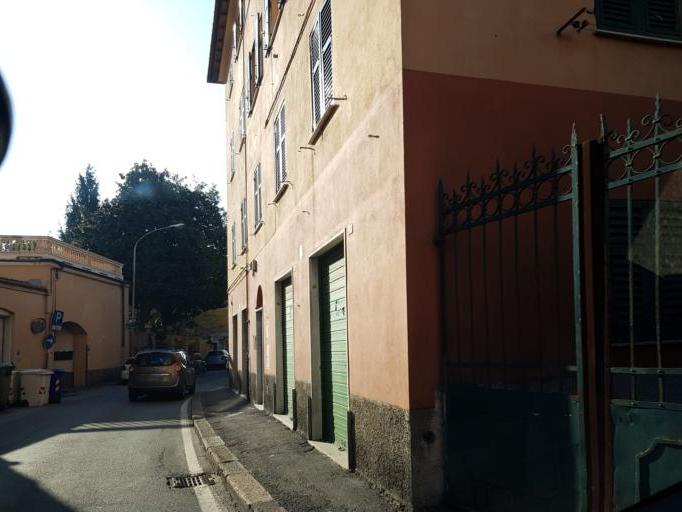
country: IT
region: Liguria
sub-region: Provincia di Genova
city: Santa Marta
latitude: 44.4943
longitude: 8.9035
